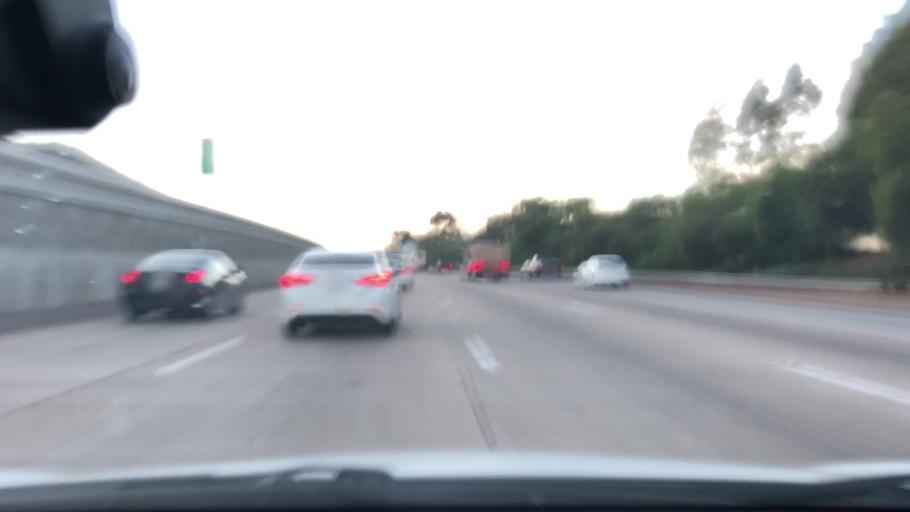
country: US
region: California
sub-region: San Diego County
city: Escondido
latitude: 33.0508
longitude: -117.0731
